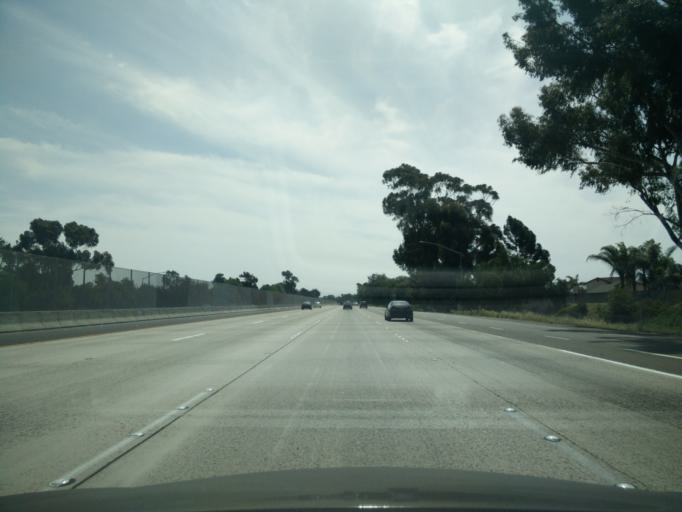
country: US
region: California
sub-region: San Diego County
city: Imperial Beach
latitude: 32.5635
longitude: -117.0709
